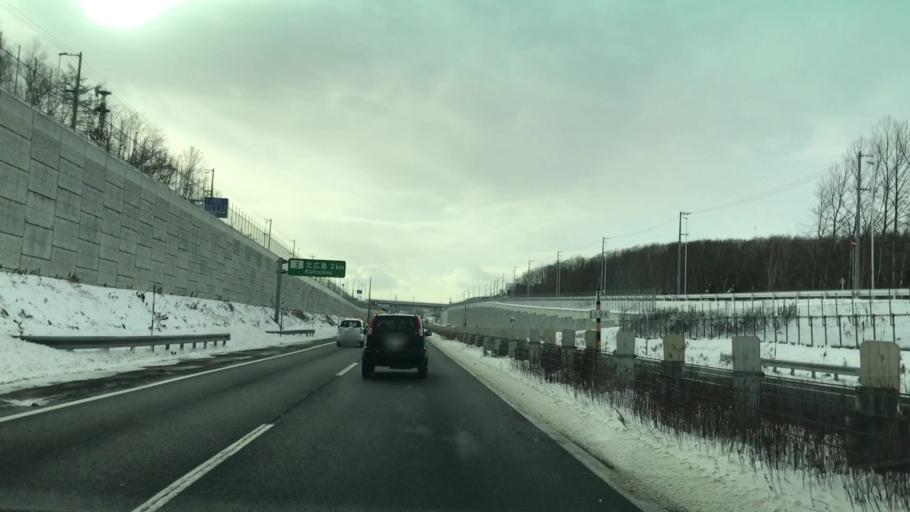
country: JP
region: Hokkaido
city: Kitahiroshima
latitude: 42.9984
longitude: 141.4683
